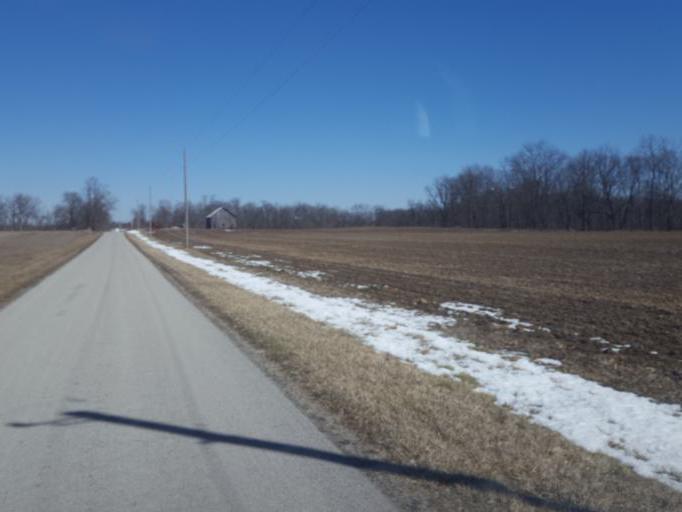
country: US
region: Ohio
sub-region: Wyandot County
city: Upper Sandusky
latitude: 40.7556
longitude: -83.1450
